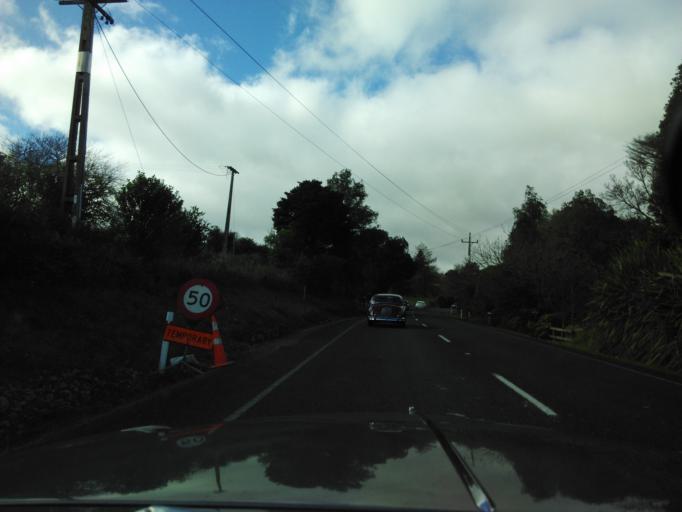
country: NZ
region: Auckland
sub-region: Auckland
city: Pukekohe East
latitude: -37.1475
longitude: 174.9941
